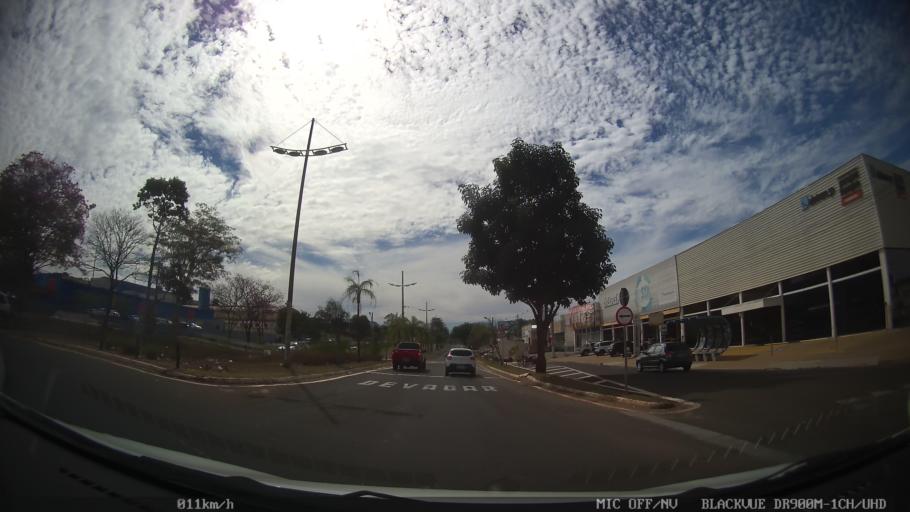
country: BR
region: Sao Paulo
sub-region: Catanduva
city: Catanduva
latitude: -21.1563
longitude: -48.9838
